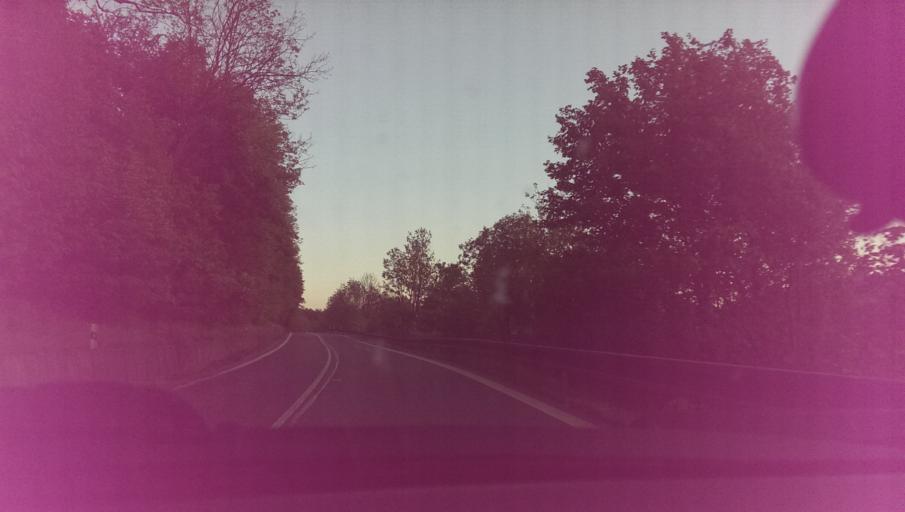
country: CZ
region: Zlin
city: Jablunka
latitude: 49.4038
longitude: 17.9536
